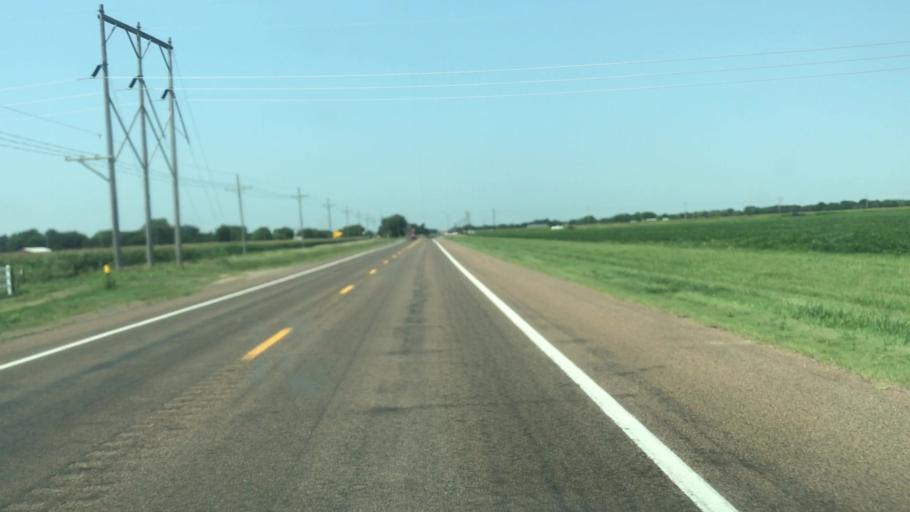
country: US
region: Nebraska
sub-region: Hall County
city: Grand Island
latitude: 40.8869
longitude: -98.3155
